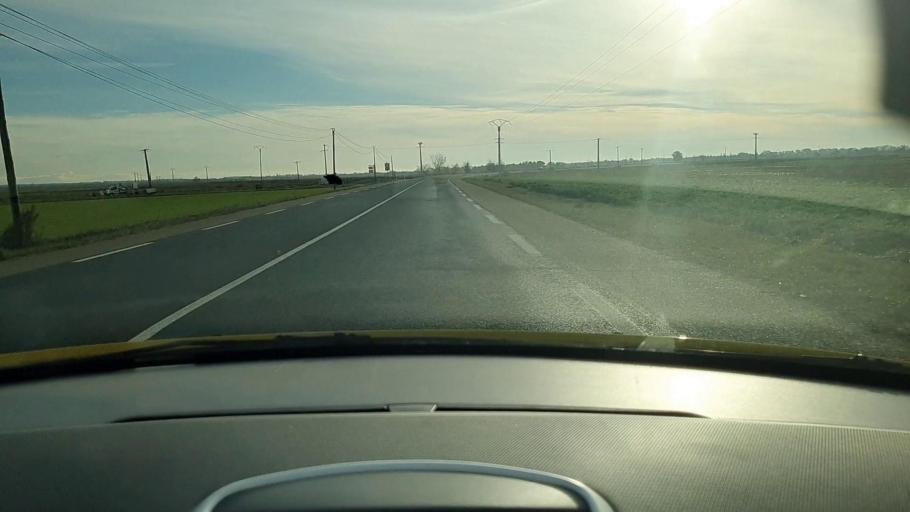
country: FR
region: Languedoc-Roussillon
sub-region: Departement du Gard
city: Bellegarde
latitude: 43.7236
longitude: 4.5442
